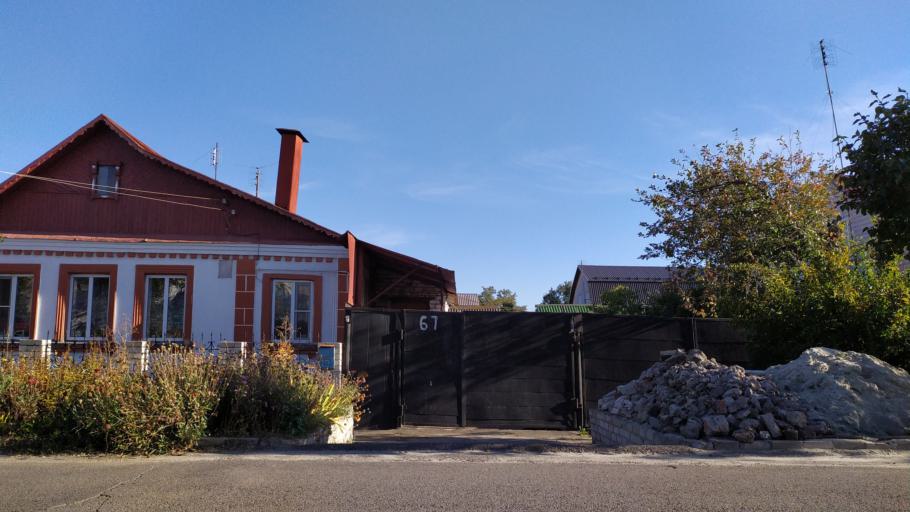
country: RU
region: Kursk
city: Kursk
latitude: 51.6463
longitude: 36.1487
